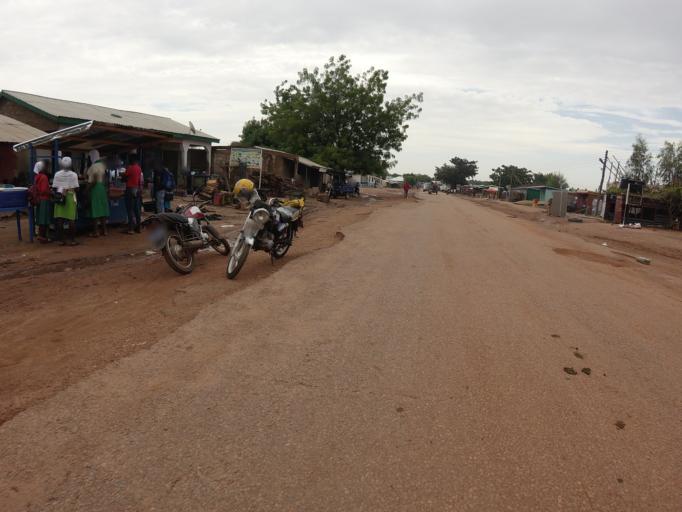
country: GH
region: Upper East
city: Bawku
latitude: 10.9376
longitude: -0.4896
